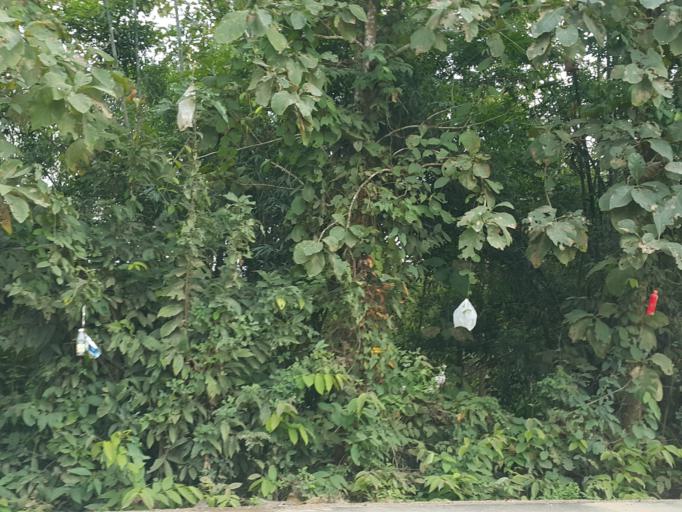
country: TH
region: Lampang
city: Chae Hom
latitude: 18.5777
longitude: 99.4550
